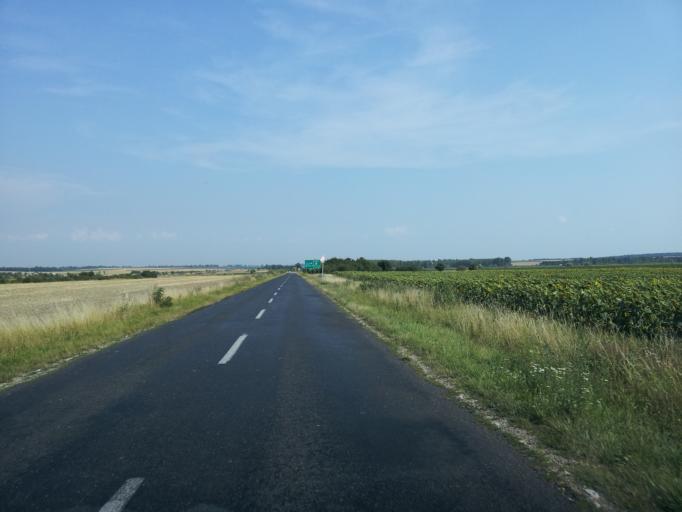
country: HU
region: Veszprem
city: Liter
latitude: 47.0837
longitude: 18.0559
